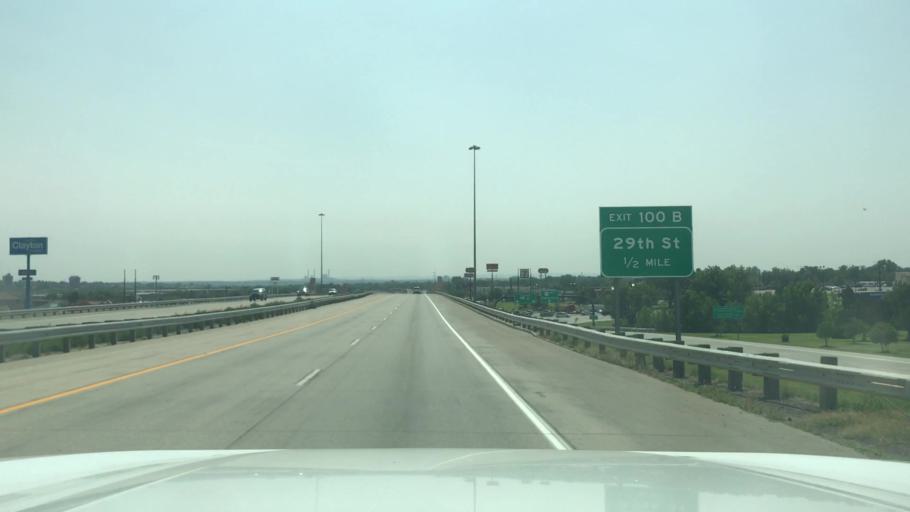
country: US
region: Colorado
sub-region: Pueblo County
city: Pueblo
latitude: 38.3102
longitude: -104.6146
